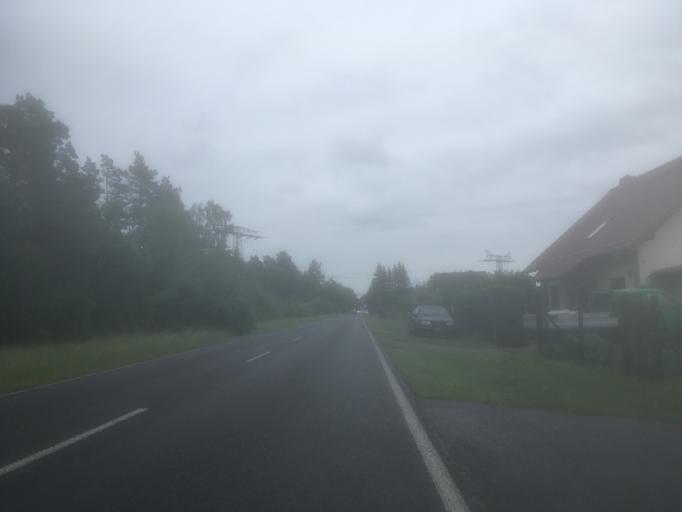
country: DE
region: Brandenburg
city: Zehdenick
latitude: 53.0099
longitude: 13.3441
